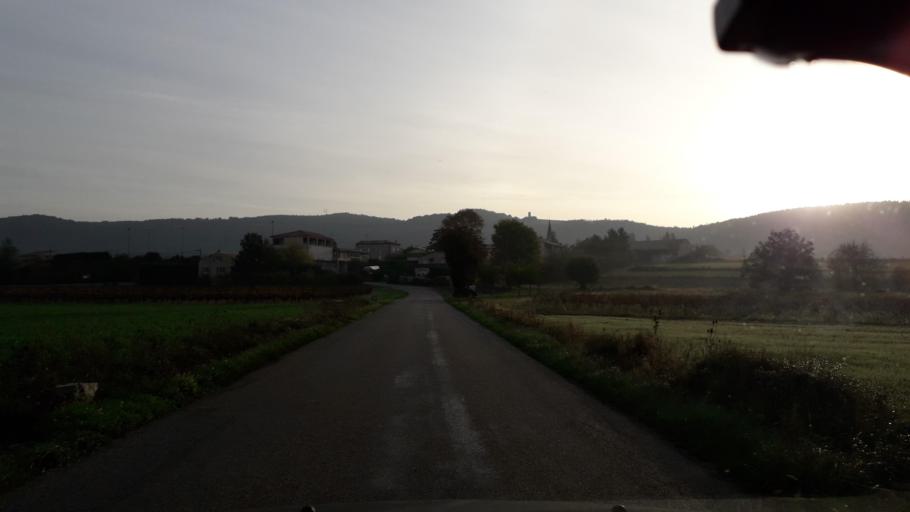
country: FR
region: Rhone-Alpes
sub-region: Departement de l'Ardeche
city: Lavilledieu
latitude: 44.6119
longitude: 4.4677
